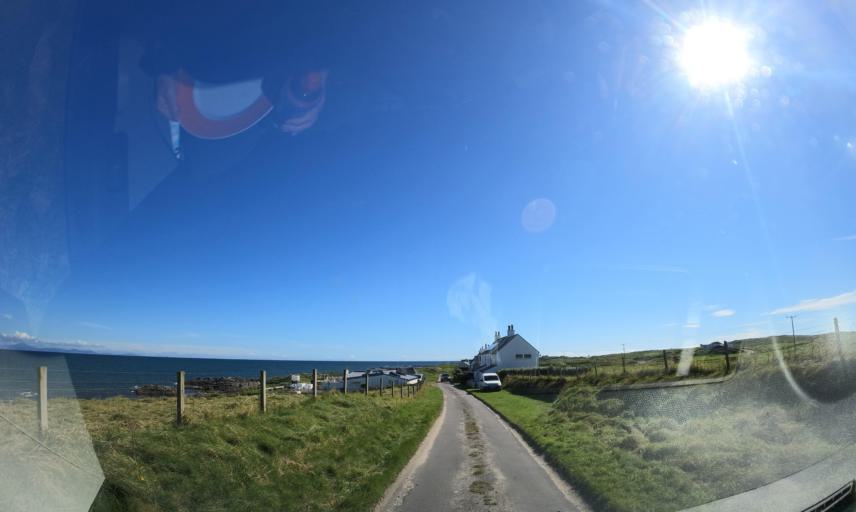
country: GB
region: Scotland
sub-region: Eilean Siar
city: Barra
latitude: 56.4653
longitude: -6.8959
